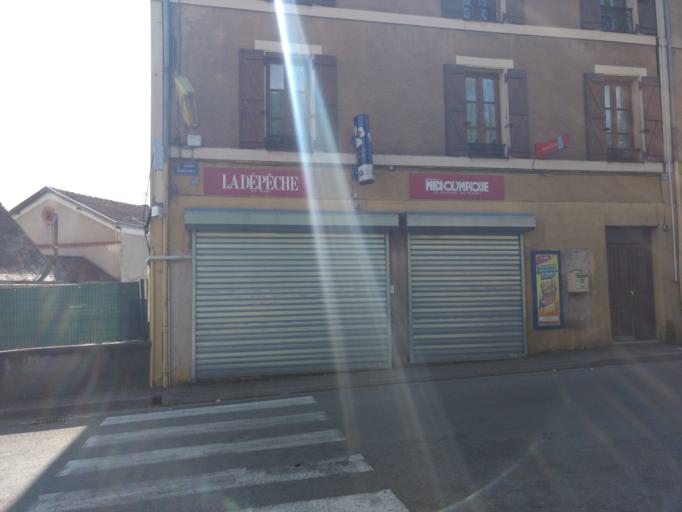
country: FR
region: Midi-Pyrenees
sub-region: Departement de l'Aveyron
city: Decazeville
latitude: 44.5638
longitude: 2.2508
